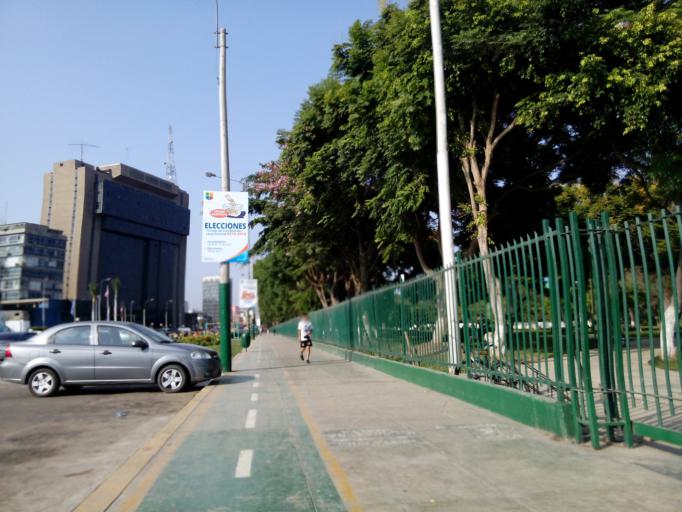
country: PE
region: Lima
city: Lima
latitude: -12.0671
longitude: -77.0422
